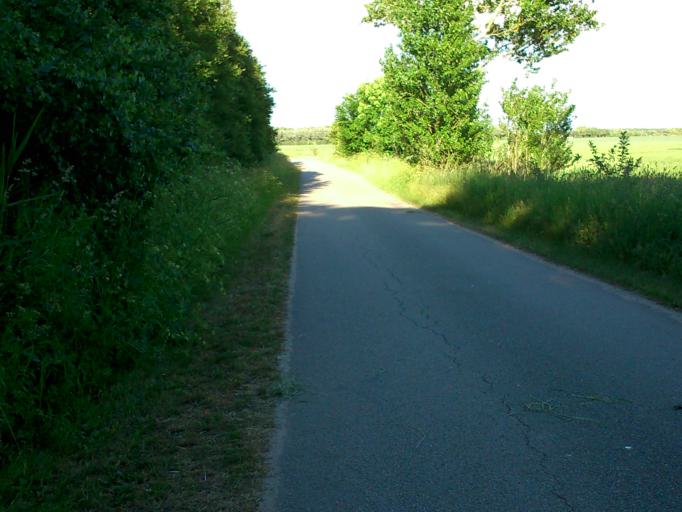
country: DK
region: Central Jutland
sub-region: Ringkobing-Skjern Kommune
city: Skjern
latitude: 55.9017
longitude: 8.4194
